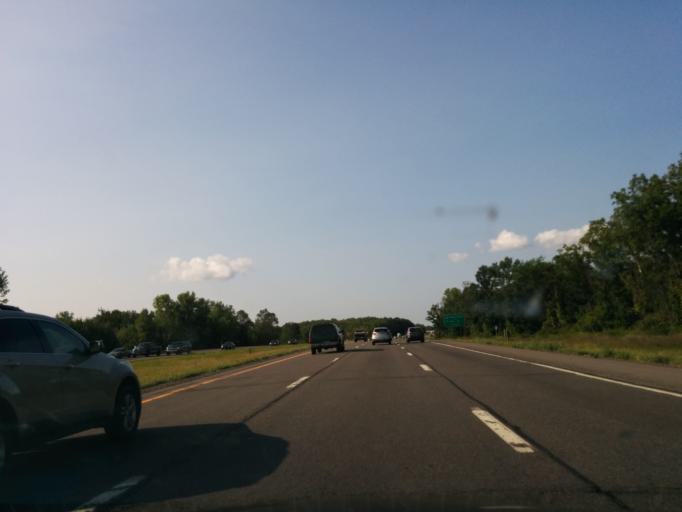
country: US
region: New York
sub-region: Onondaga County
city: Brewerton
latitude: 43.2178
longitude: -76.1296
